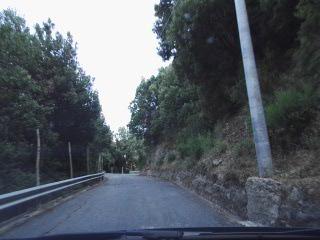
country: IT
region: Calabria
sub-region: Provincia di Vibo-Valentia
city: Nardodipace
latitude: 38.4379
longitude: 16.3381
